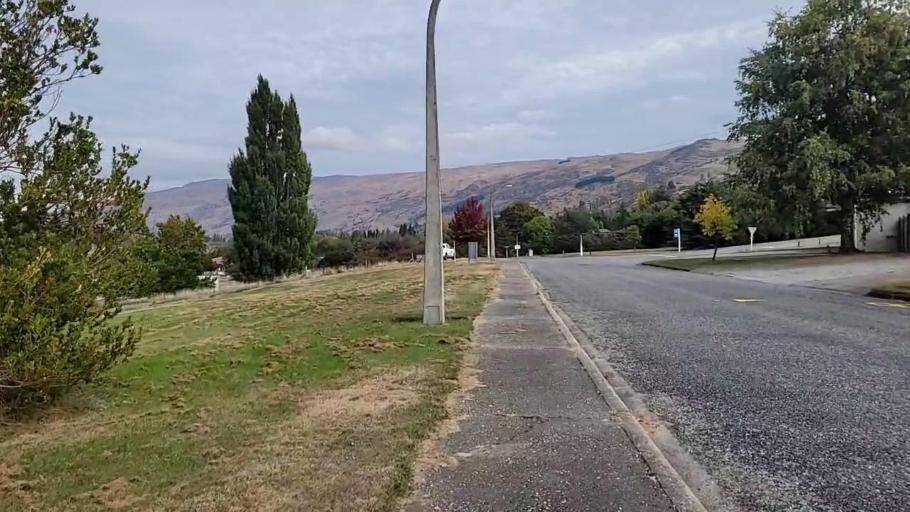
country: NZ
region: Otago
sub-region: Queenstown-Lakes District
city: Kingston
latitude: -45.4772
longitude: 169.3176
